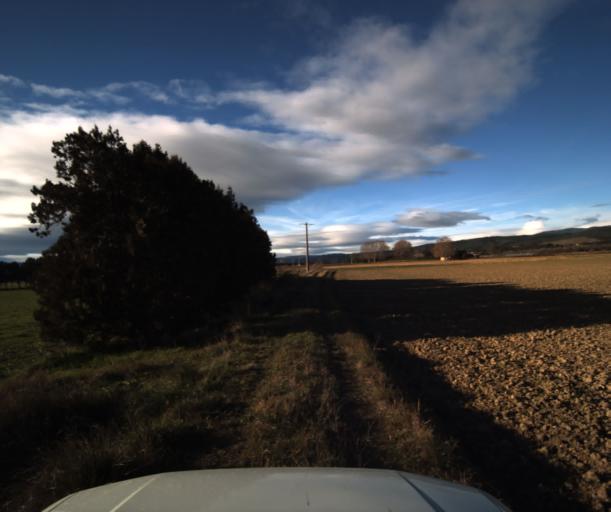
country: FR
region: Provence-Alpes-Cote d'Azur
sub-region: Departement du Vaucluse
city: Pertuis
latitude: 43.6849
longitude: 5.4698
